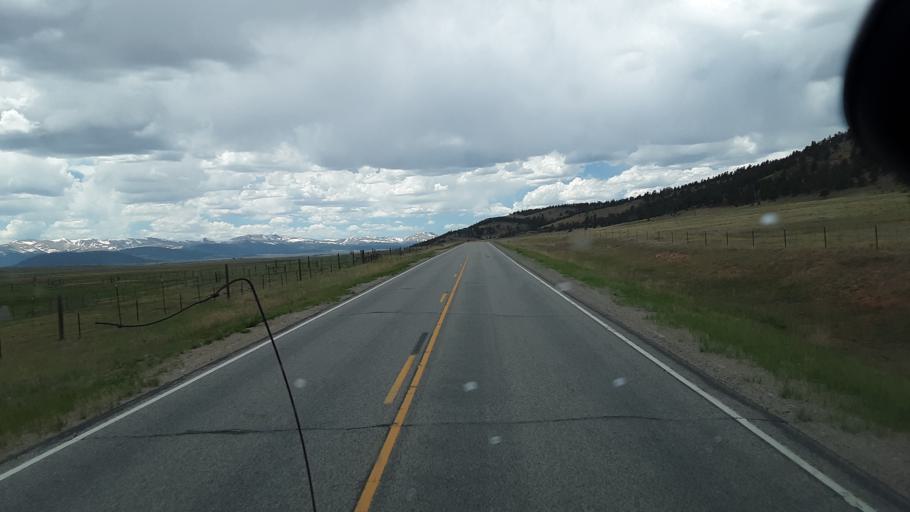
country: US
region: Colorado
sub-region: Park County
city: Fairplay
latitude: 39.0365
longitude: -105.8254
